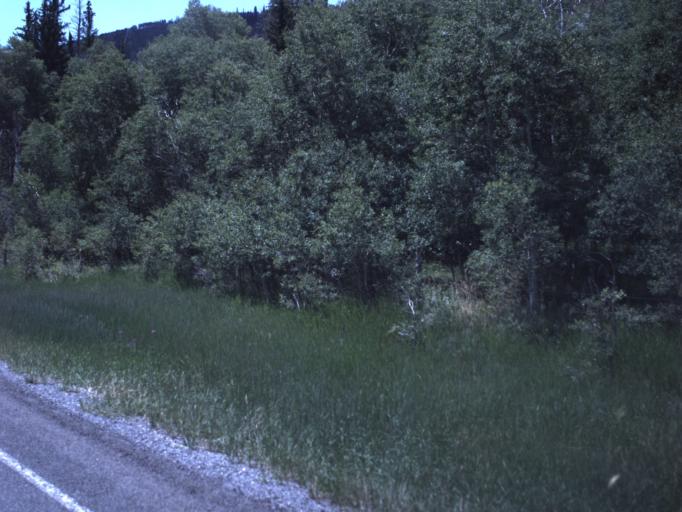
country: US
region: Utah
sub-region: Sanpete County
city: Fairview
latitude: 39.7104
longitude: -111.1633
